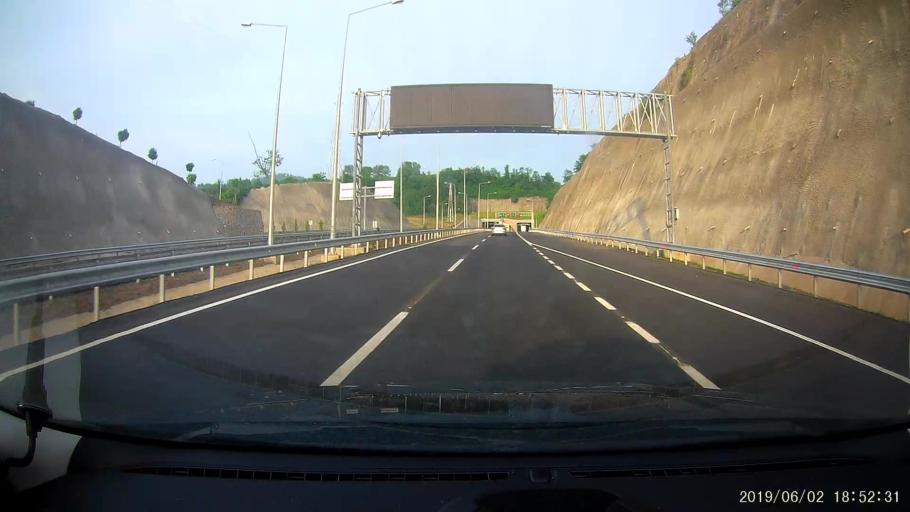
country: TR
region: Ordu
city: Ordu
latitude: 40.9885
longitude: 37.8139
